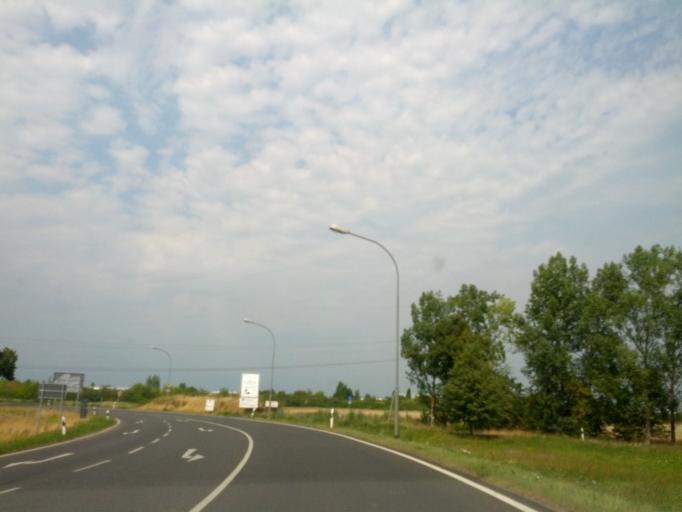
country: DE
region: Brandenburg
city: Nauen
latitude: 52.5918
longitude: 12.8910
